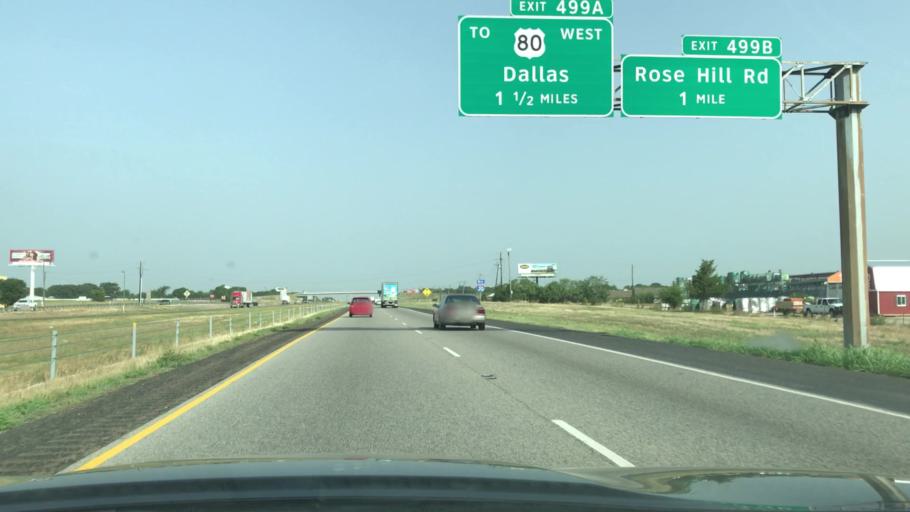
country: US
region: Texas
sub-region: Kaufman County
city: Terrell
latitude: 32.7043
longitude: -96.2815
